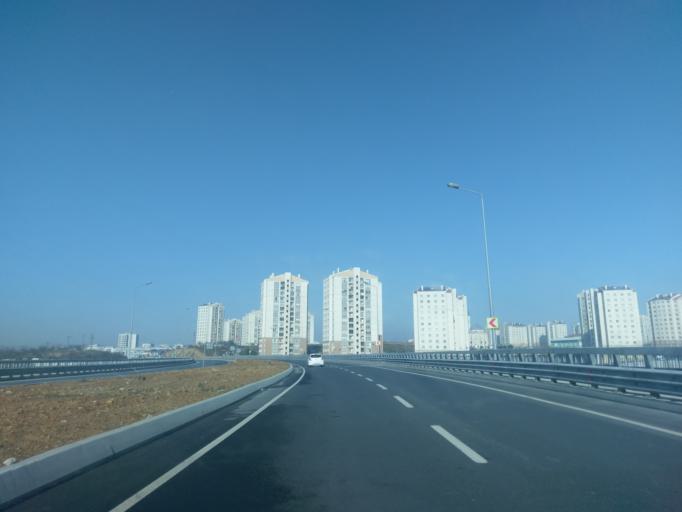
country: TR
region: Istanbul
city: Basaksehir
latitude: 41.1286
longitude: 28.7917
